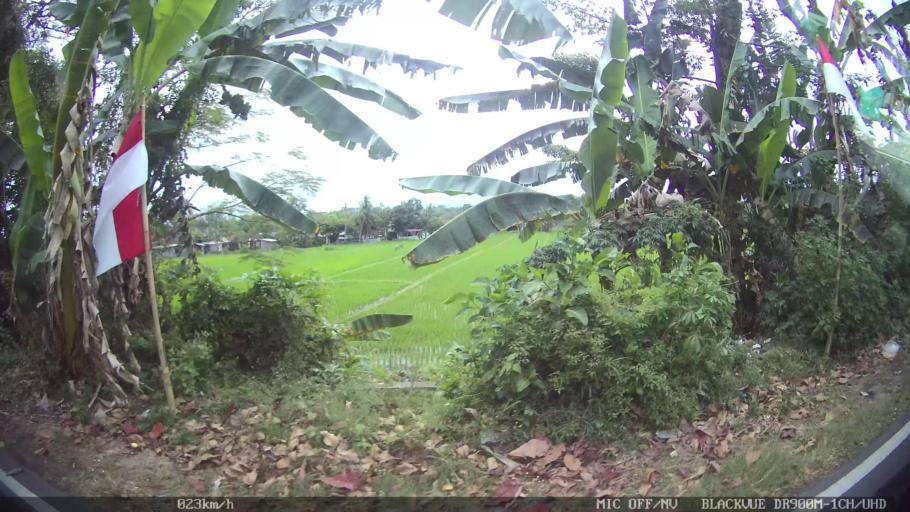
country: ID
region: Central Java
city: Candi Prambanan
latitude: -7.7700
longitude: 110.4838
